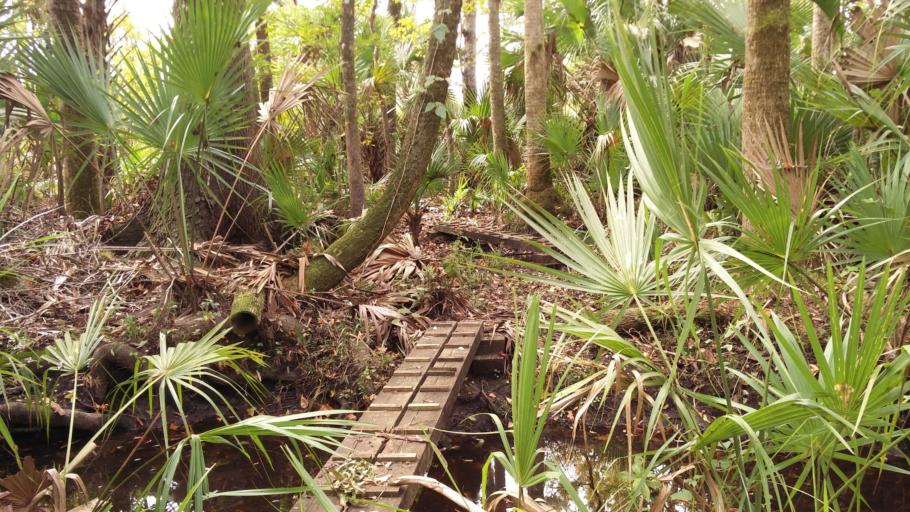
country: US
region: Florida
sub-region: Brevard County
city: June Park
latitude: 28.0841
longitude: -80.9343
